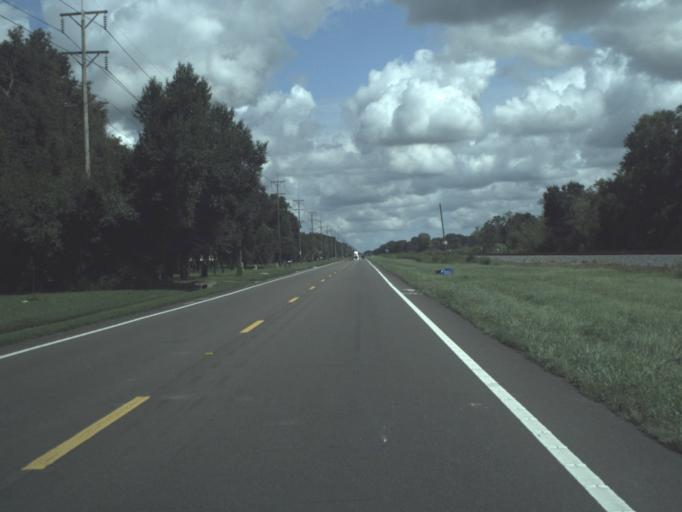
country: US
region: Florida
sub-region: Pasco County
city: Crystal Springs
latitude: 28.1142
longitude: -82.1451
